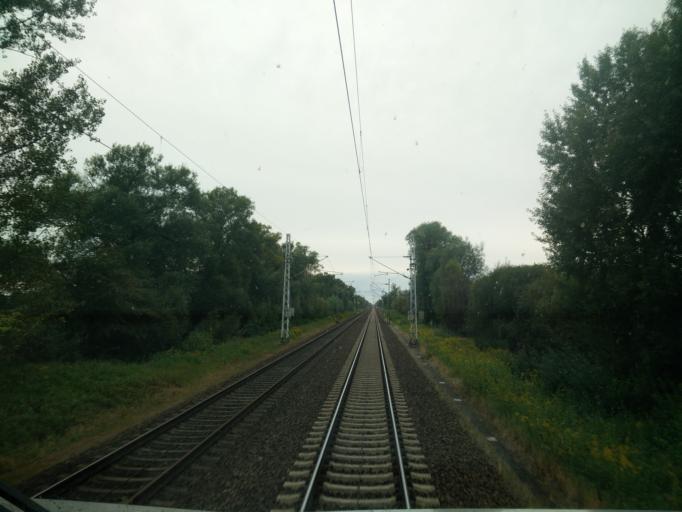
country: DE
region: Brandenburg
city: Nauen
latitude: 52.6332
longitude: 12.8273
